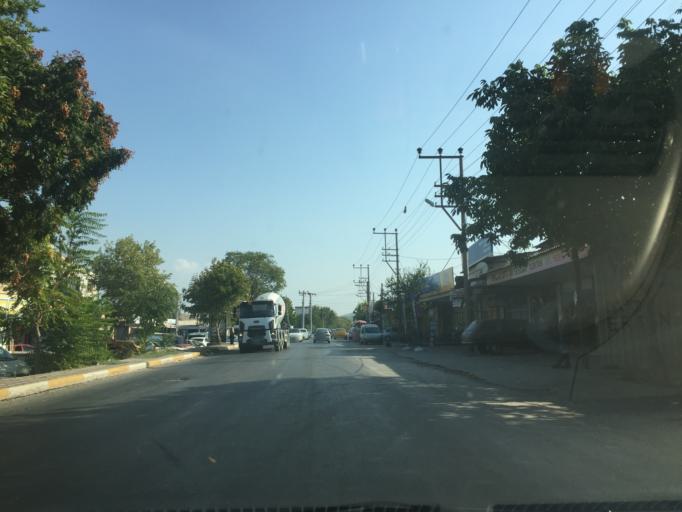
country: TR
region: Manisa
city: Akhisar
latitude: 38.9087
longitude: 27.8370
